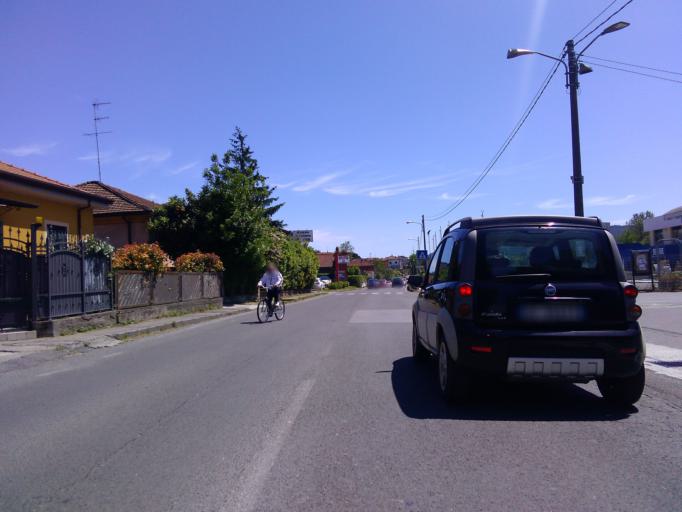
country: IT
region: Liguria
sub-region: Provincia di La Spezia
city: Sarzana
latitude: 44.1281
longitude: 9.9426
